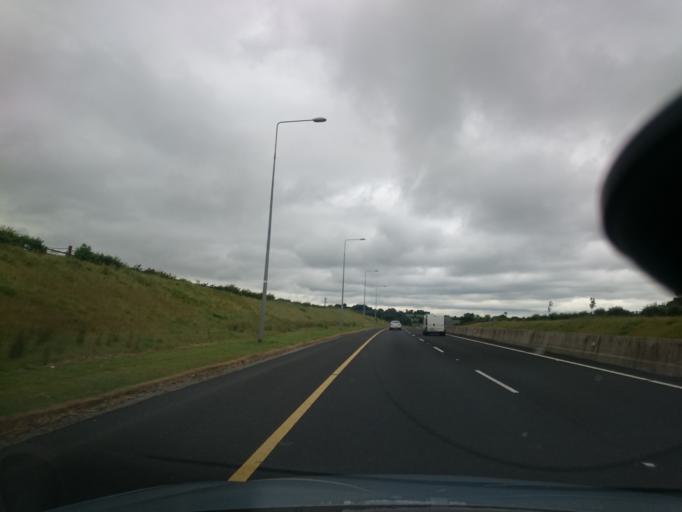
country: IE
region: Leinster
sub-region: Kildare
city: Moone
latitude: 53.0046
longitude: -6.8395
